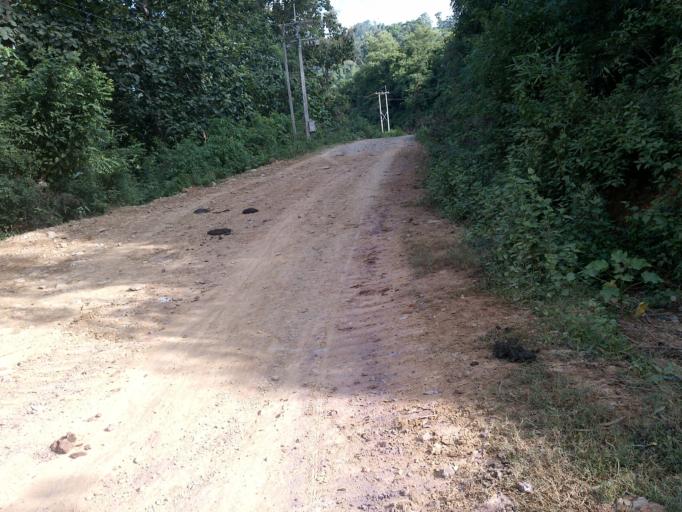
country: TH
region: Nan
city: Chaloem Phra Kiat
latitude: 19.9190
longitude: 101.1621
